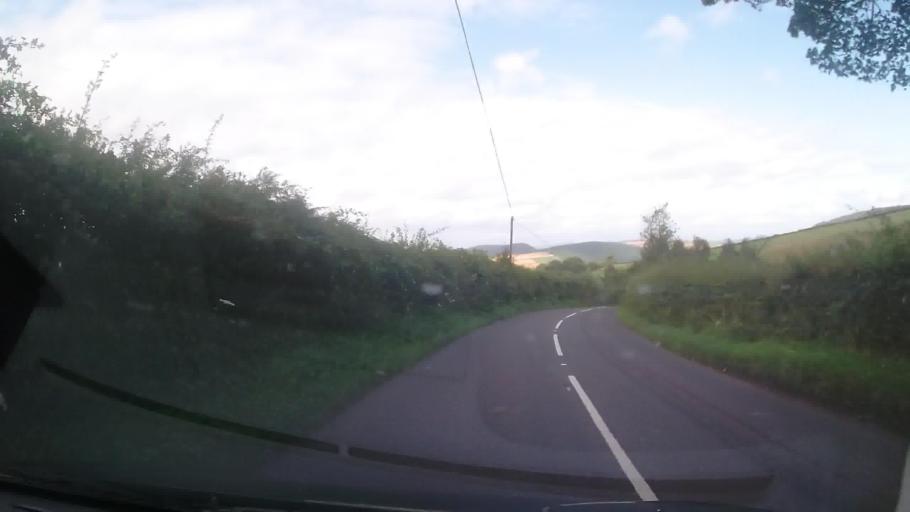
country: GB
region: England
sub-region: Shropshire
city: Acton
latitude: 52.4067
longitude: -3.0447
